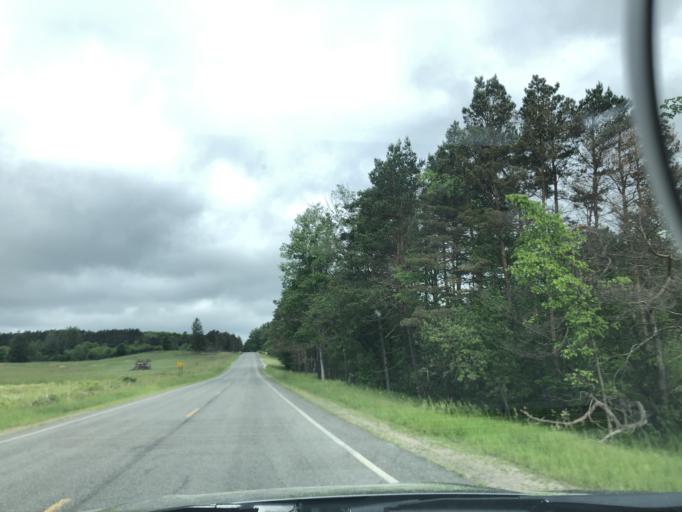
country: US
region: Michigan
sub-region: Missaukee County
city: Lake City
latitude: 44.4538
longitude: -85.2093
